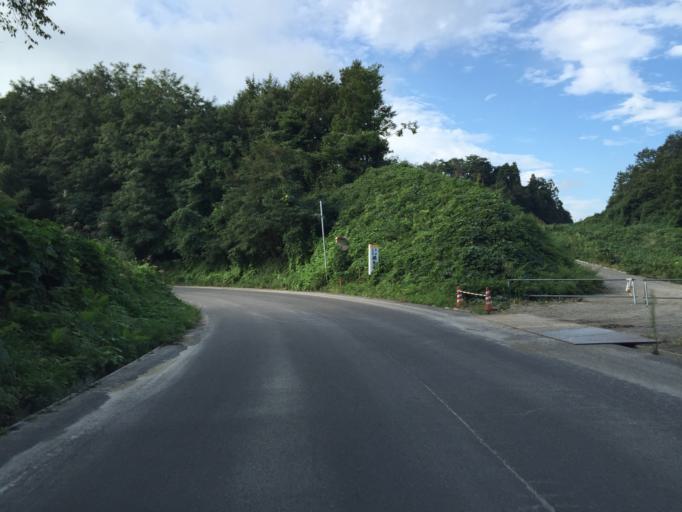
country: JP
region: Fukushima
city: Fukushima-shi
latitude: 37.6556
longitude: 140.5764
